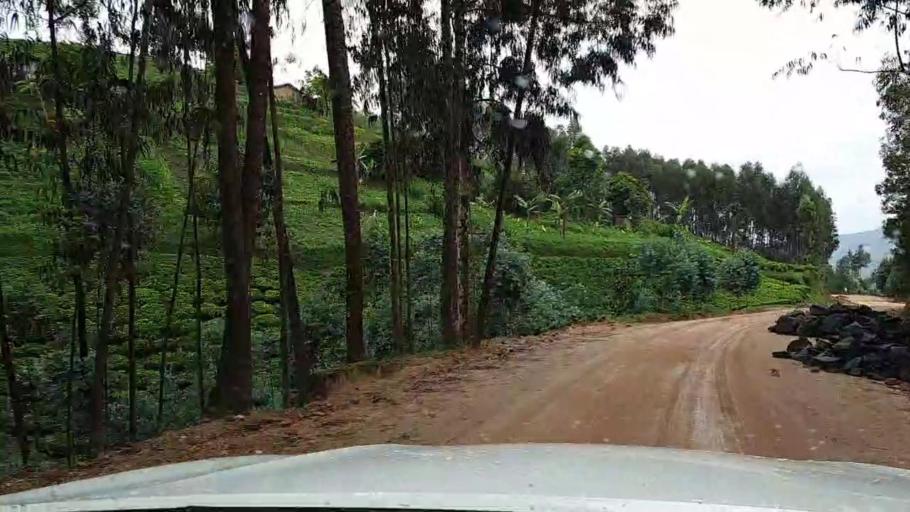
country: RW
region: Southern Province
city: Nzega
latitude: -2.4560
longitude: 29.4659
